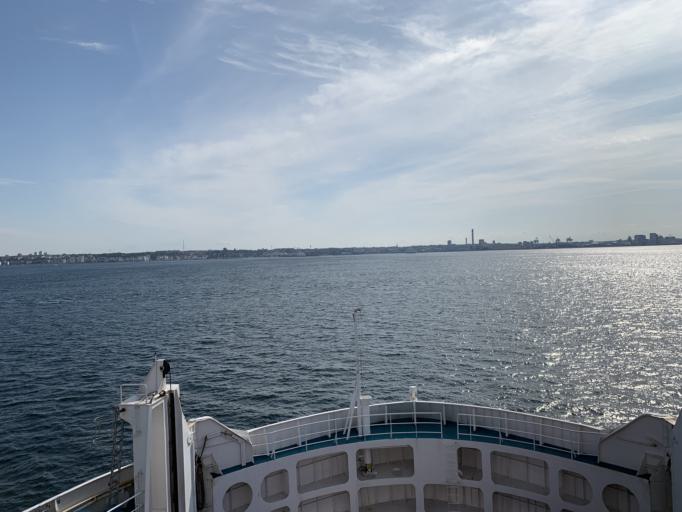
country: DK
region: Capital Region
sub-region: Helsingor Kommune
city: Helsingor
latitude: 56.0363
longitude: 12.6453
